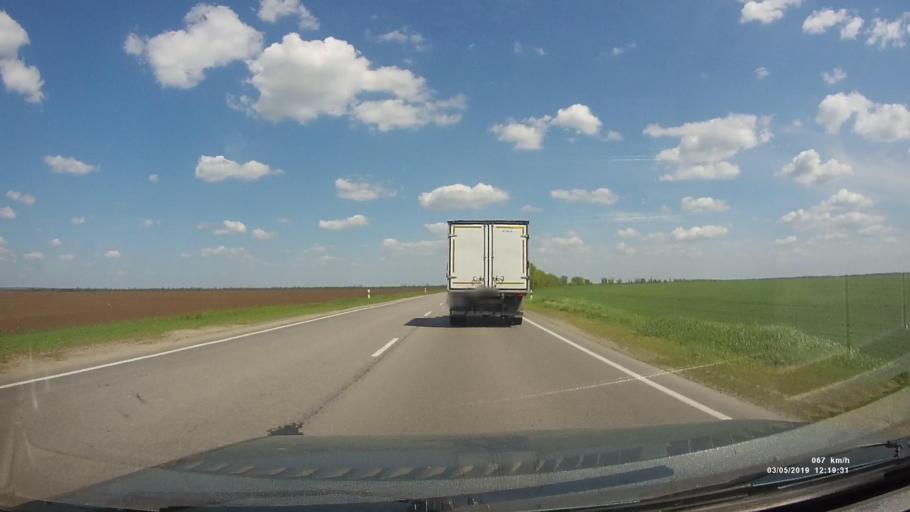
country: RU
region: Rostov
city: Melikhovskaya
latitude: 47.4010
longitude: 40.6087
